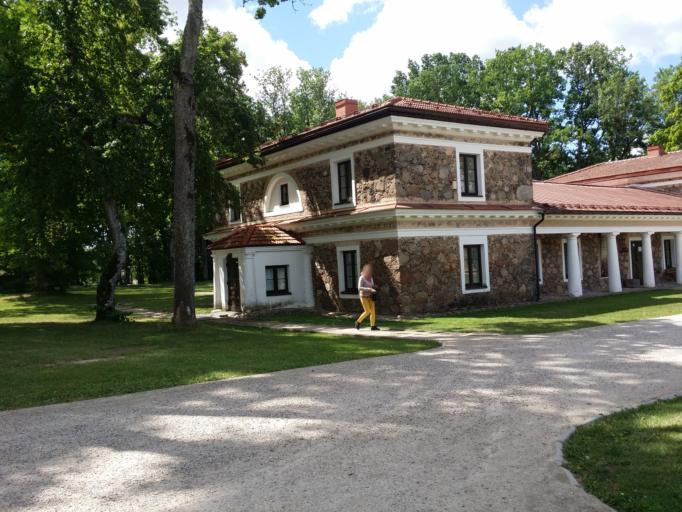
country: LT
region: Panevezys
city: Rokiskis
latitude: 55.9652
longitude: 25.6005
